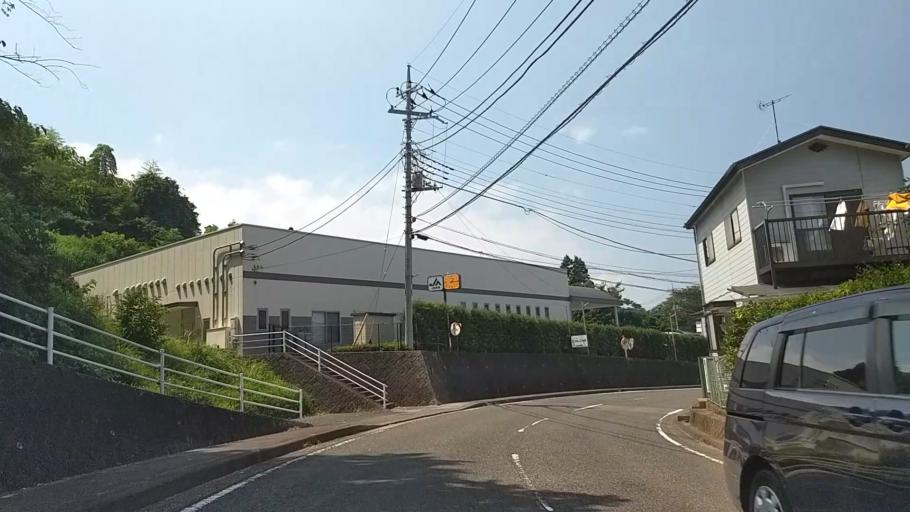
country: JP
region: Shizuoka
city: Ito
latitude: 34.9432
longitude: 139.1136
